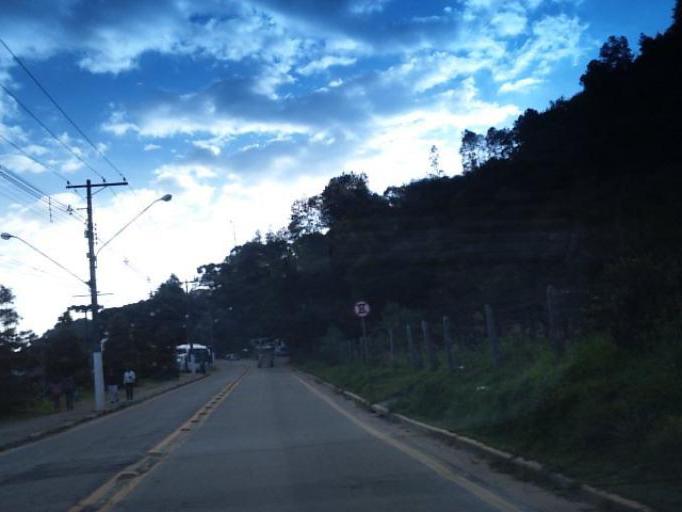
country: BR
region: Sao Paulo
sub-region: Campos Do Jordao
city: Campos do Jordao
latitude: -22.7166
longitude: -45.5668
